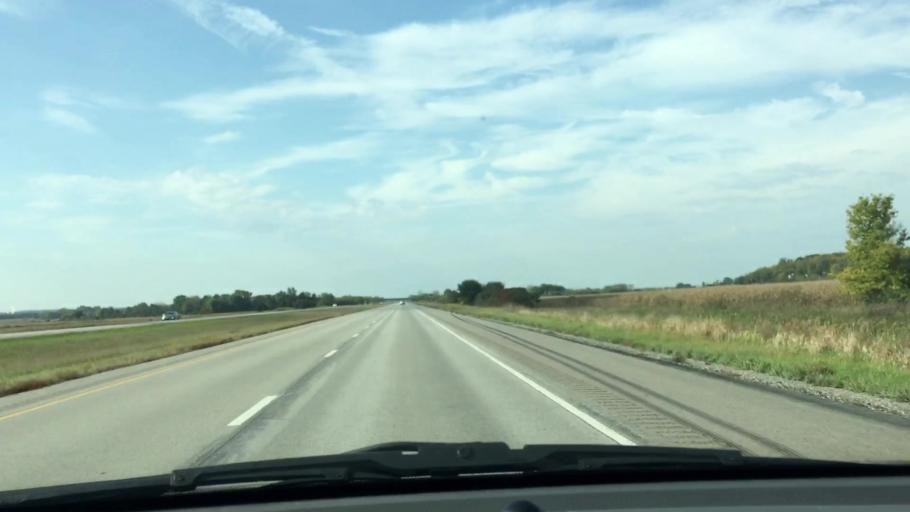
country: US
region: Illinois
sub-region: Rock Island County
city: Port Byron
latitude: 41.5818
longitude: -90.2091
